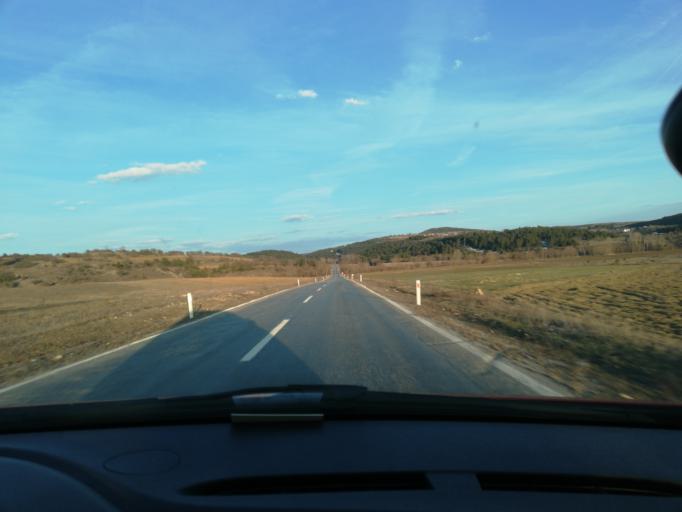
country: TR
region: Kastamonu
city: Agli
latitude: 41.6953
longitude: 33.6119
